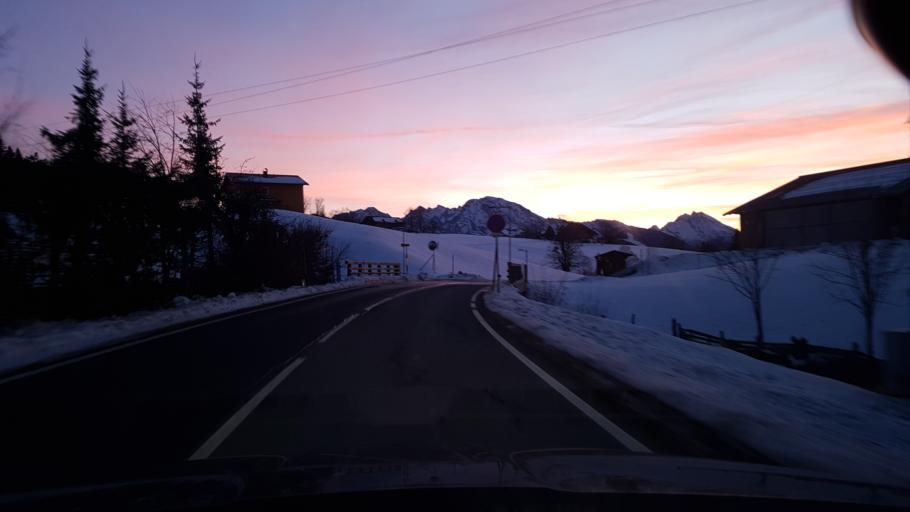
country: AT
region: Salzburg
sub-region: Politischer Bezirk Hallein
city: Krispl
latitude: 47.7120
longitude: 13.1732
